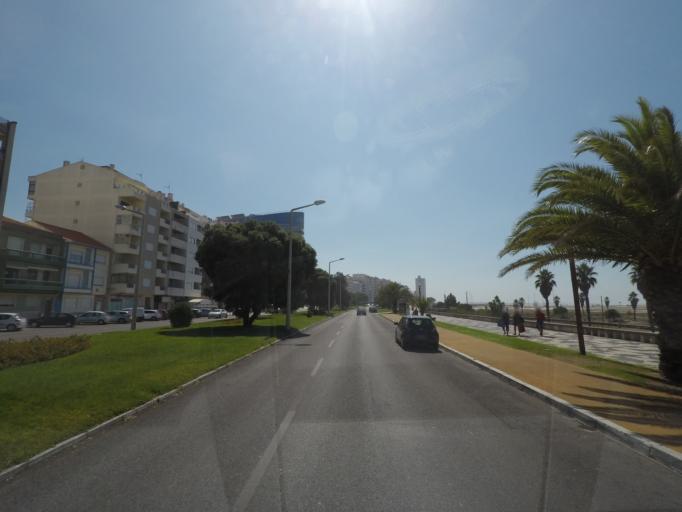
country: PT
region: Coimbra
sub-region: Figueira da Foz
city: Figueira da Foz
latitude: 40.1574
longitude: -8.8687
